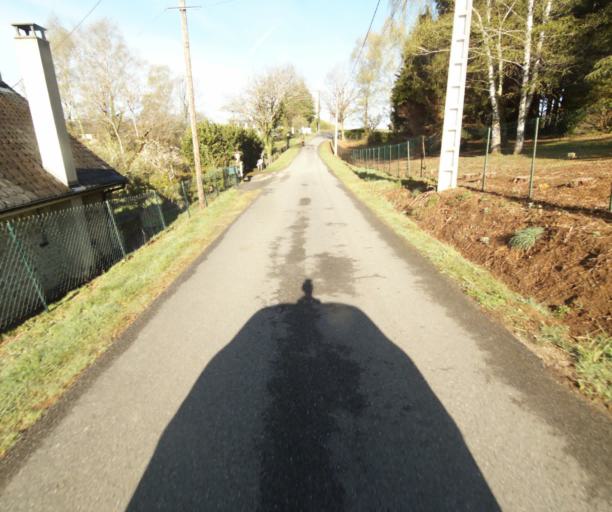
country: FR
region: Limousin
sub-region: Departement de la Correze
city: Laguenne
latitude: 45.2850
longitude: 1.8492
